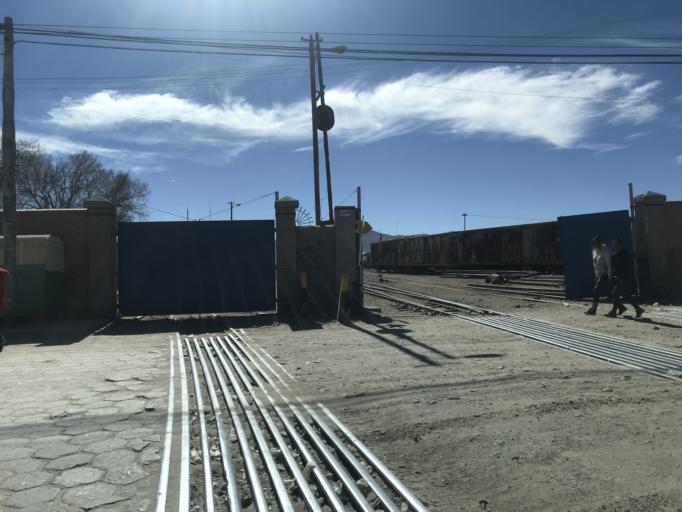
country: BO
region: Potosi
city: Uyuni
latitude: -20.4658
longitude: -66.8239
